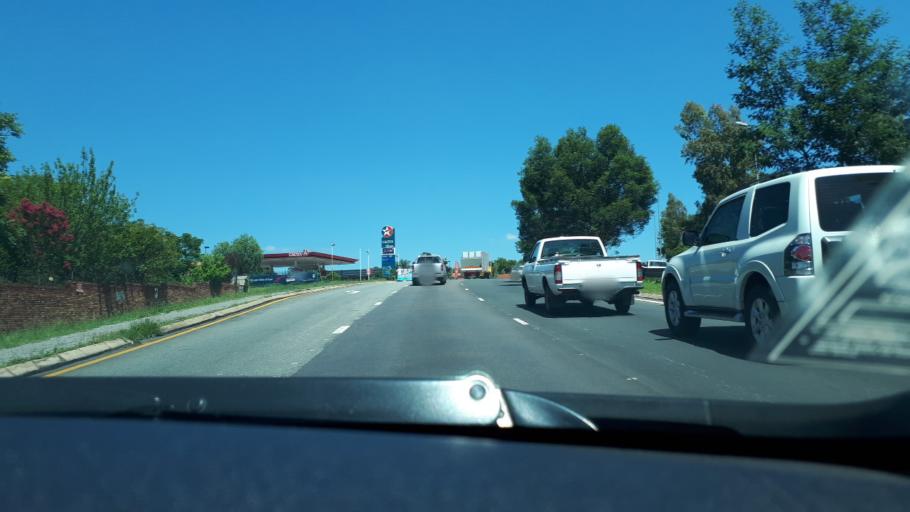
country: ZA
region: Gauteng
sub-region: West Rand District Municipality
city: Muldersdriseloop
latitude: -26.0677
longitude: 27.9636
